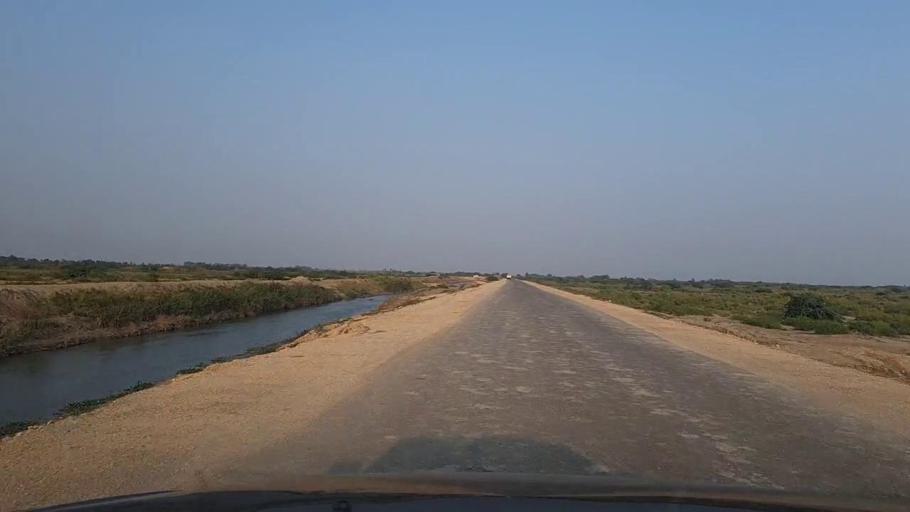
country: PK
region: Sindh
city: Mirpur Sakro
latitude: 24.4431
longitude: 67.7829
